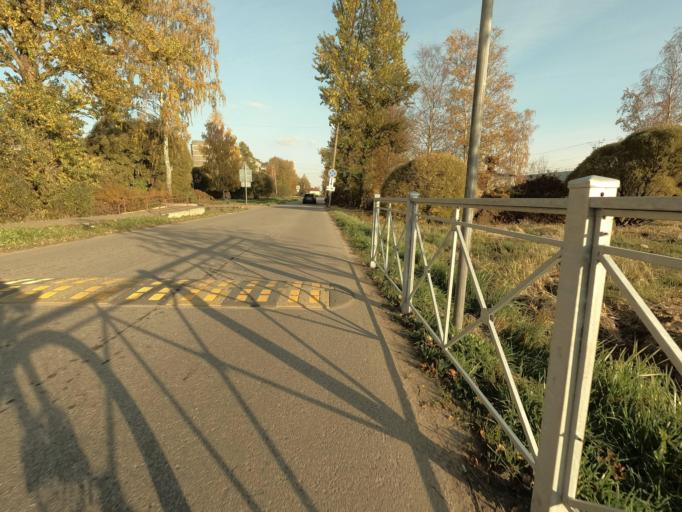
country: RU
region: Leningrad
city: Mga
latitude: 59.7575
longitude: 31.0520
